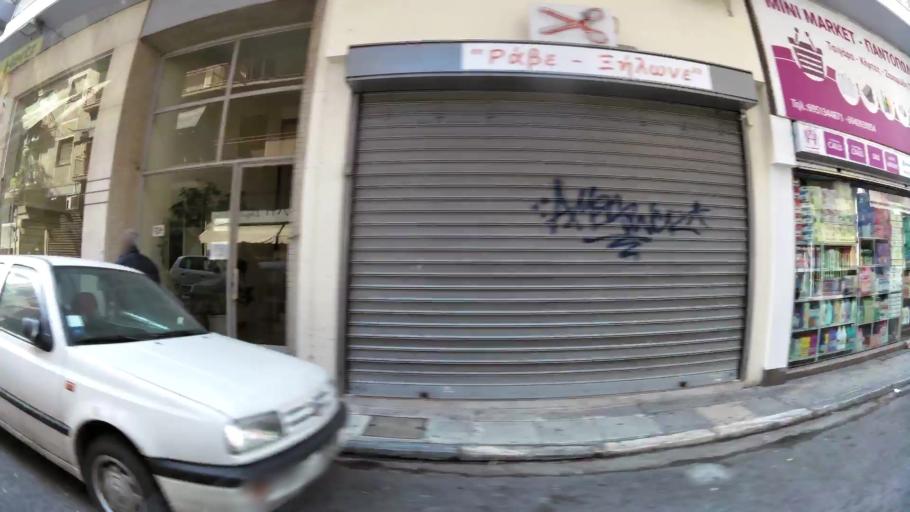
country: GR
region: Attica
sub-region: Nomarchia Athinas
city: Kipseli
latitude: 38.0003
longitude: 23.7200
